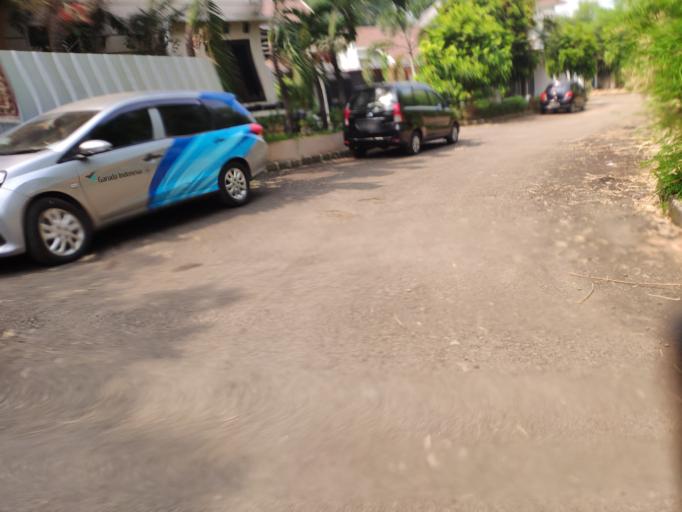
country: ID
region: West Java
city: Pamulang
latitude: -6.3242
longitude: 106.8051
